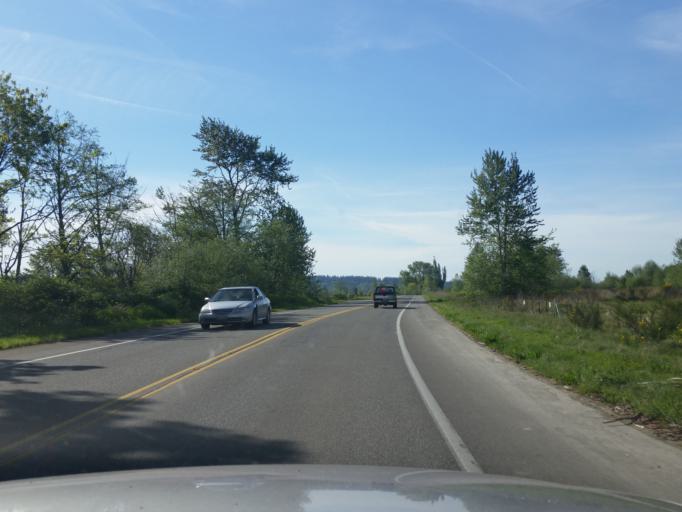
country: US
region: Washington
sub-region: Snohomish County
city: Fobes Hill
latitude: 47.9214
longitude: -122.1508
